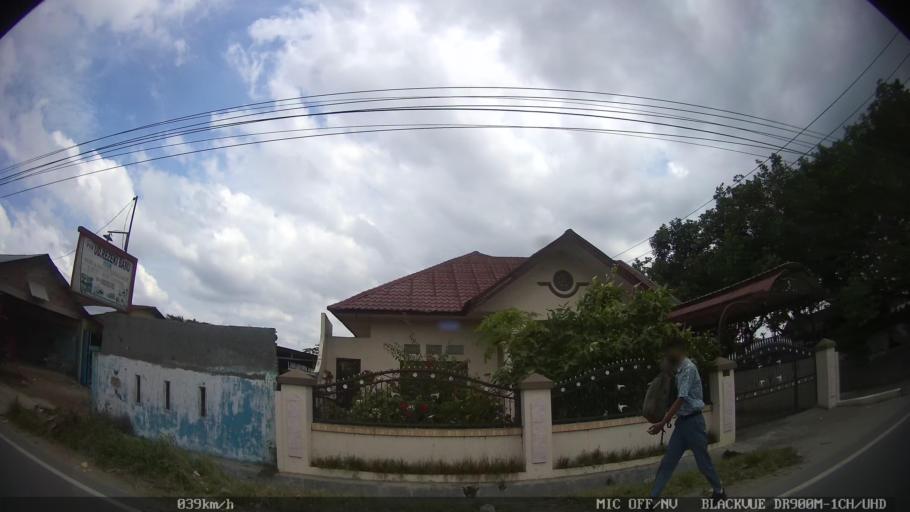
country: ID
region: North Sumatra
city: Sunggal
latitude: 3.6180
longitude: 98.6214
